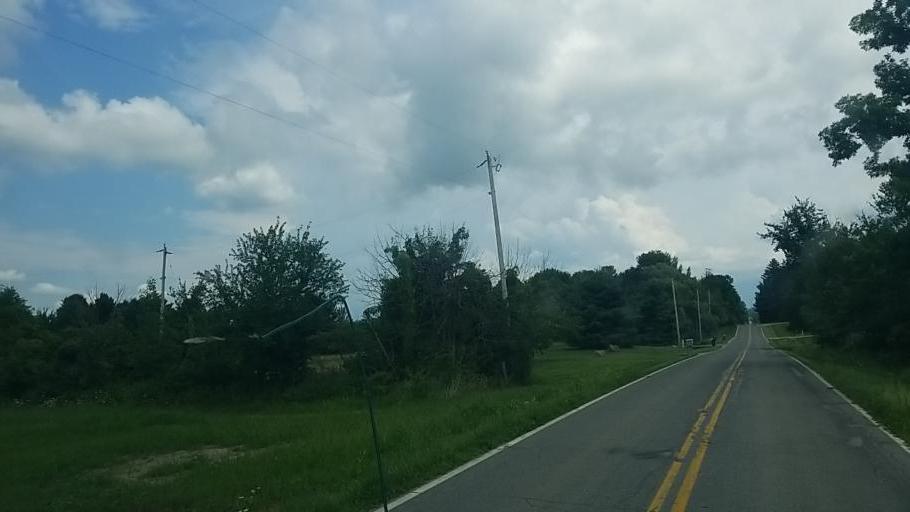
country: US
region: Ohio
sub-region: Medina County
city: Medina
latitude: 41.1423
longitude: -81.9595
